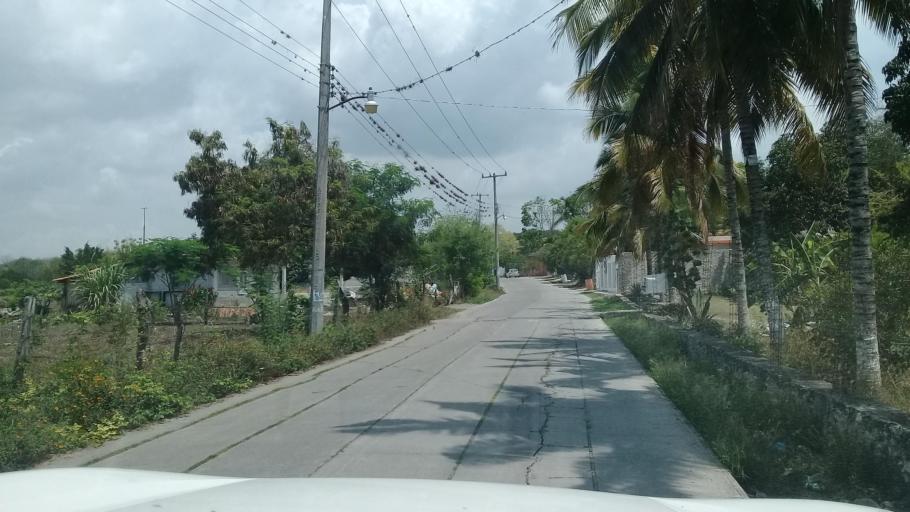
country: MX
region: Veracruz
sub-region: Emiliano Zapata
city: Plan del Rio
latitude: 19.3536
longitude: -96.6469
